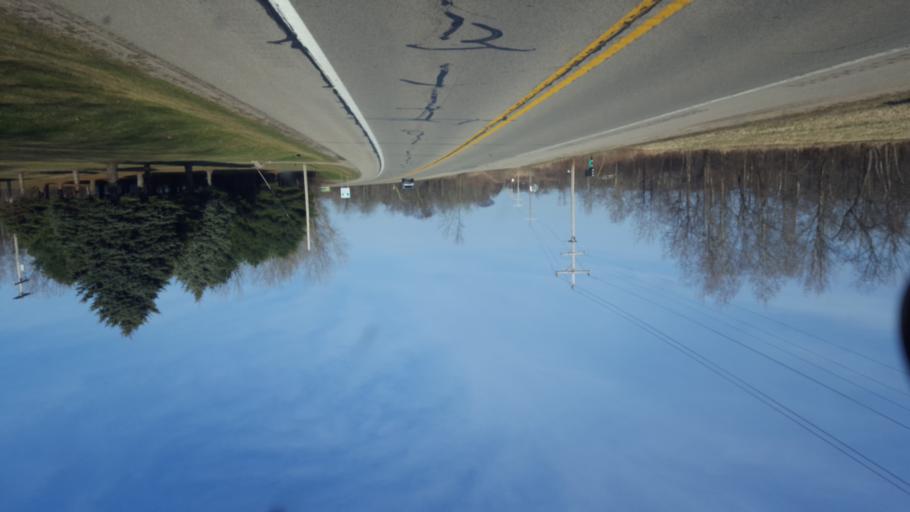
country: US
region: Michigan
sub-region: Montcalm County
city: Edmore
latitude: 43.4081
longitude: -85.1121
